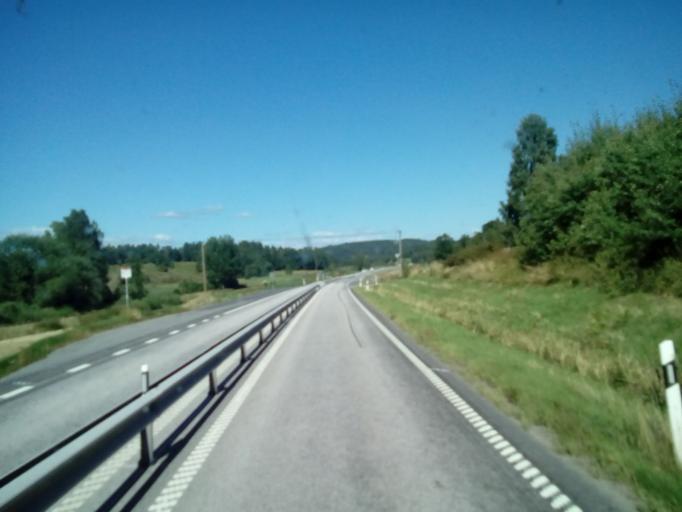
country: SE
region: OEstergoetland
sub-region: Kinda Kommun
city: Kisa
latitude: 58.0400
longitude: 15.6625
